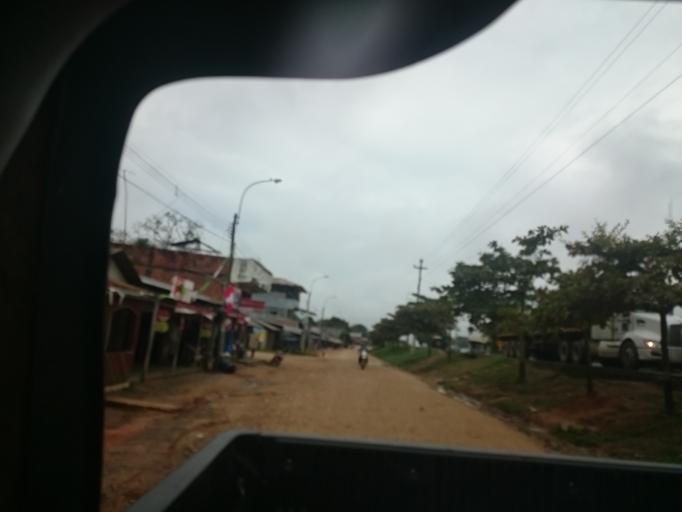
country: PE
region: Ucayali
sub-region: Provincia de Coronel Portillo
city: Campoverde
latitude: -8.4743
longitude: -74.8050
